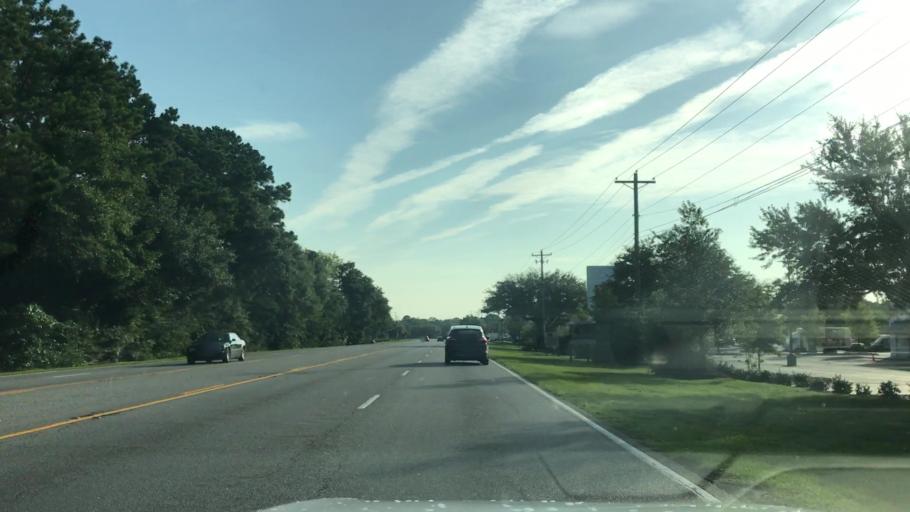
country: US
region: South Carolina
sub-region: Charleston County
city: North Charleston
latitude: 32.8135
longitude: -79.9990
